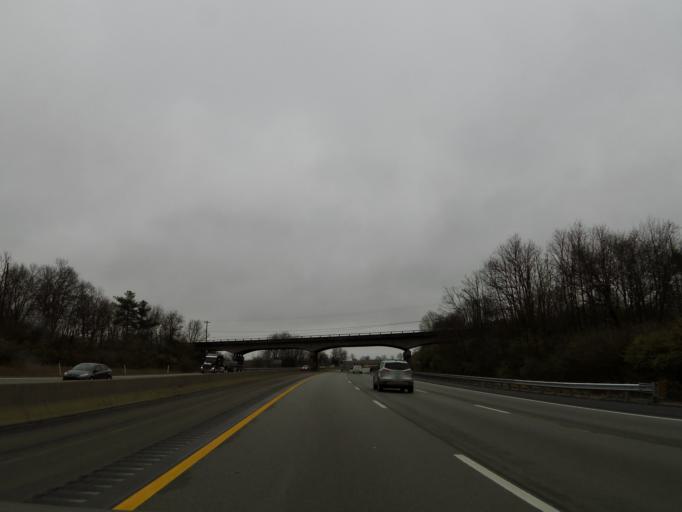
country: US
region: Kentucky
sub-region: Scott County
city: Georgetown
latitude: 38.1947
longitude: -84.5250
